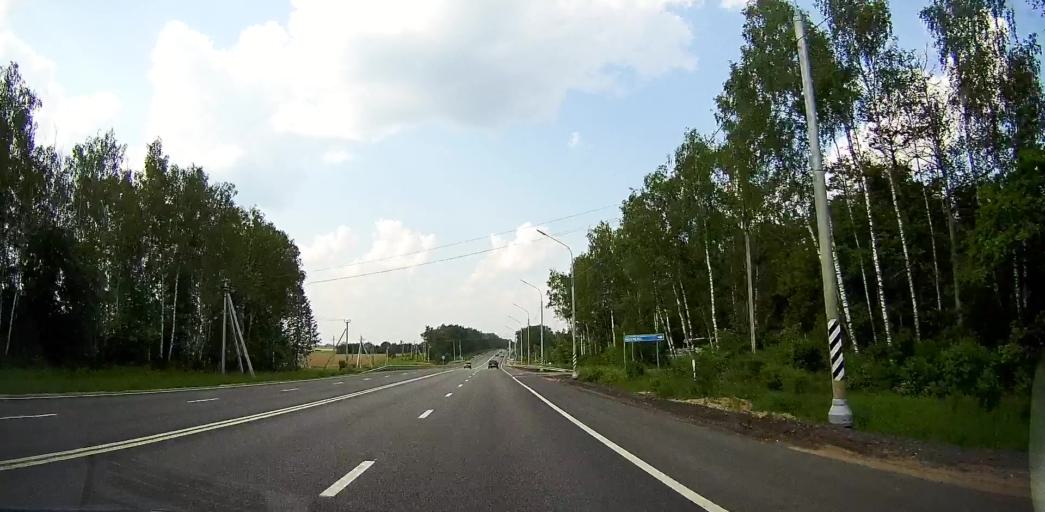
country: RU
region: Moskovskaya
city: Mikhnevo
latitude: 55.0933
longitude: 37.9527
